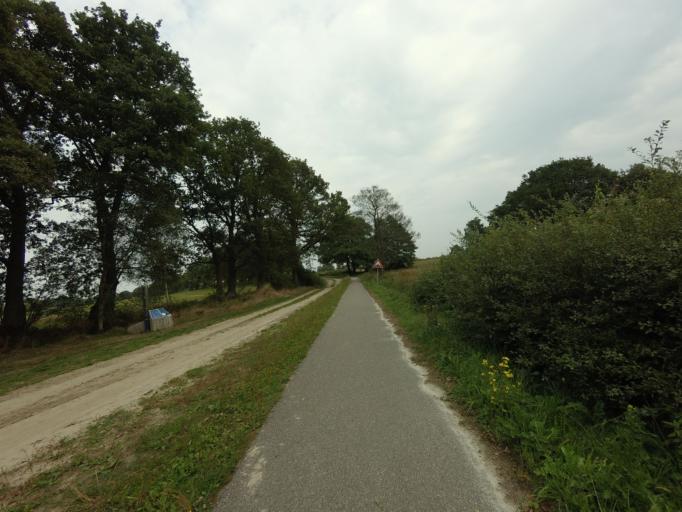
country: NL
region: Drenthe
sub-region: Gemeente Tynaarlo
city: Tynaarlo
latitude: 53.0091
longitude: 6.6338
